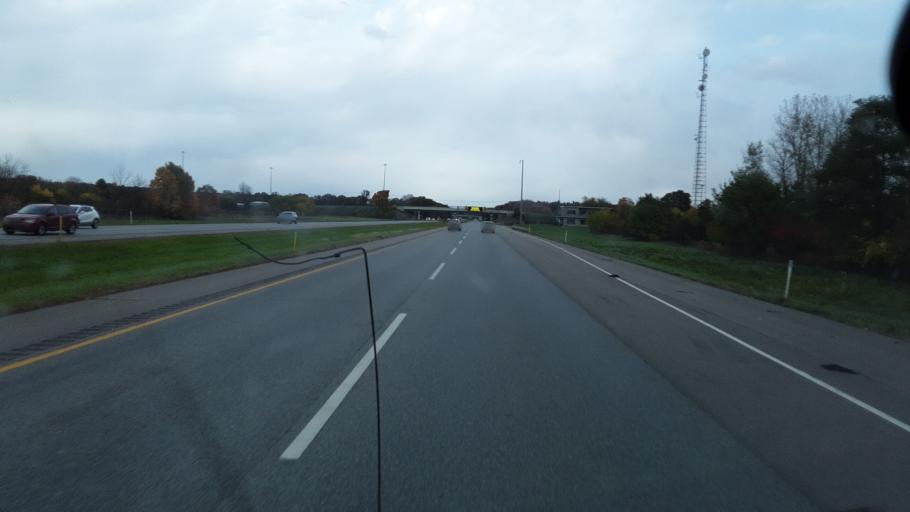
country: US
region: Indiana
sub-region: Saint Joseph County
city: Granger
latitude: 41.7312
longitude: -86.0673
